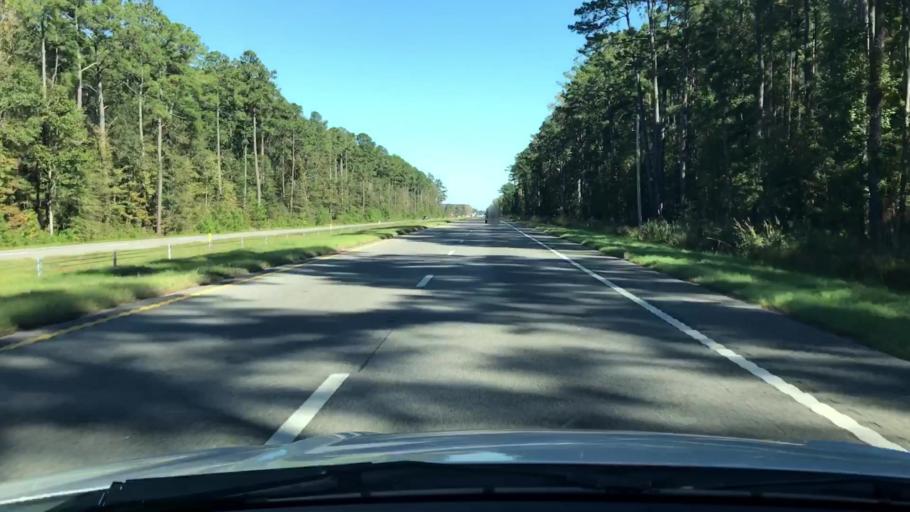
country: US
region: South Carolina
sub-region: Colleton County
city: Walterboro
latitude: 32.7647
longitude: -80.5074
